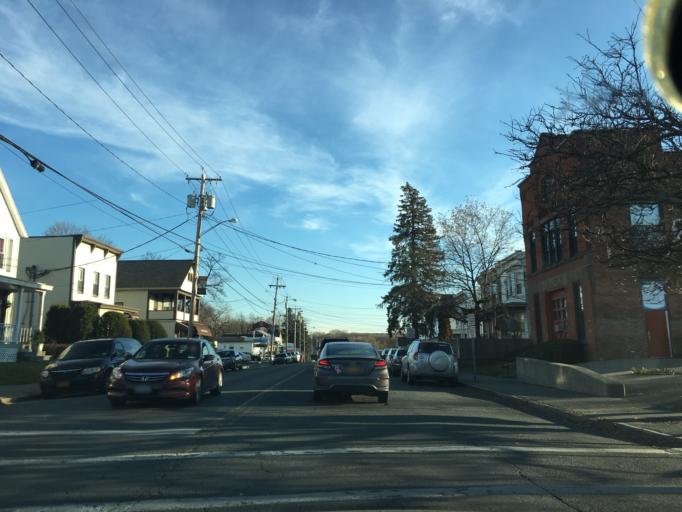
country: US
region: New York
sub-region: Rensselaer County
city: Wynantskill
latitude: 42.7052
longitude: -73.6599
